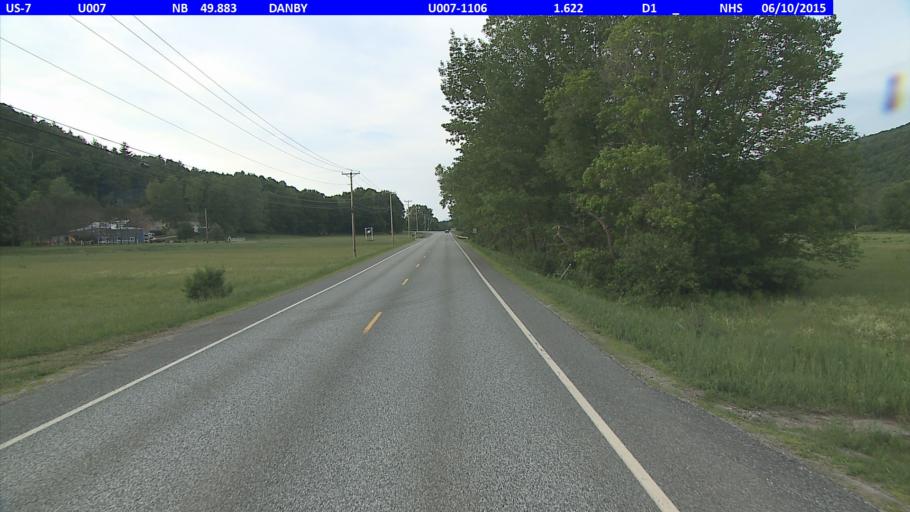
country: US
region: Vermont
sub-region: Rutland County
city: West Rutland
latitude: 43.3854
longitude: -72.9980
